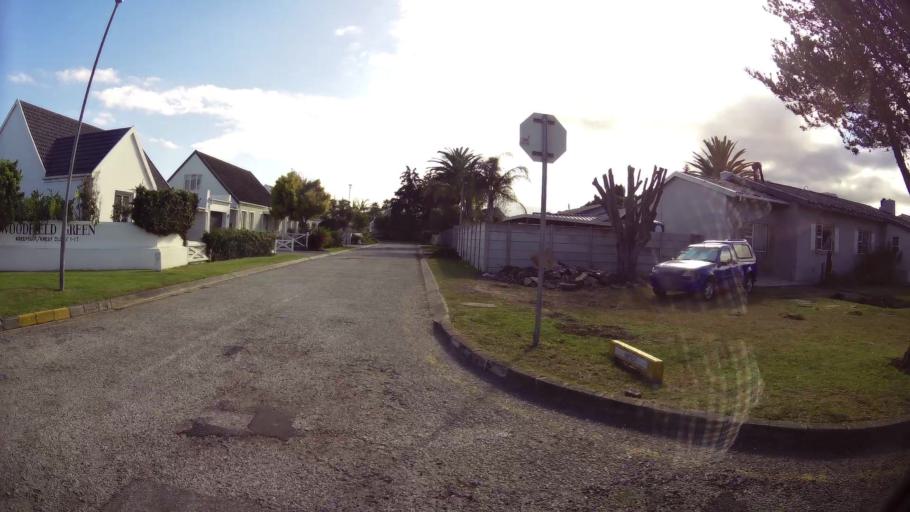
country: ZA
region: Western Cape
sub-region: Eden District Municipality
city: George
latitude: -33.9616
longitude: 22.4885
